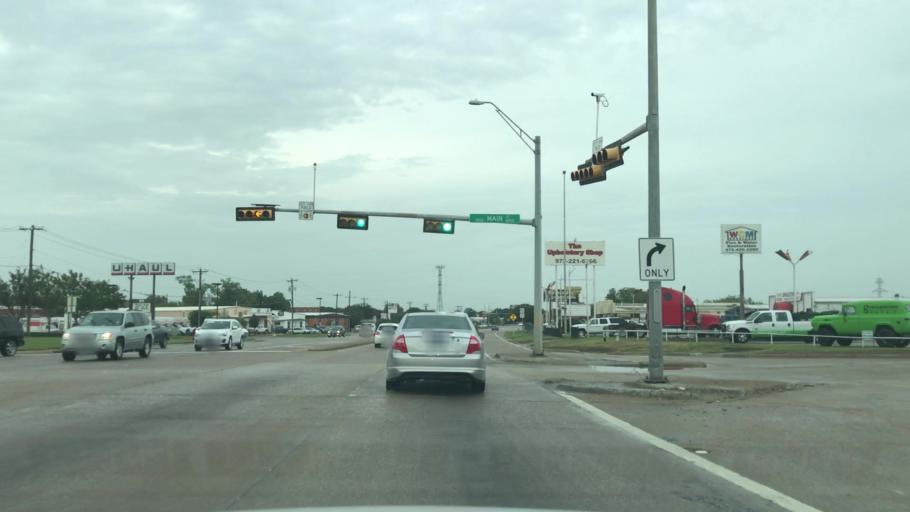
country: US
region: Texas
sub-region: Denton County
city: Lewisville
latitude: 33.0429
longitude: -96.9812
